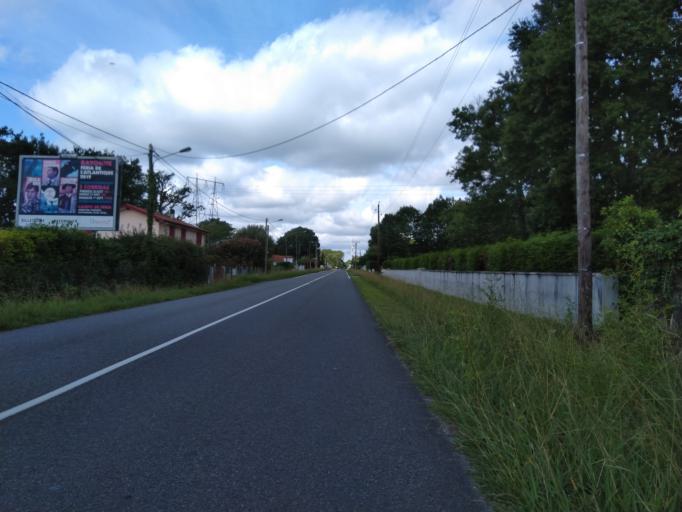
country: FR
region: Aquitaine
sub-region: Departement des Landes
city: Mees
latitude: 43.7311
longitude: -1.0964
